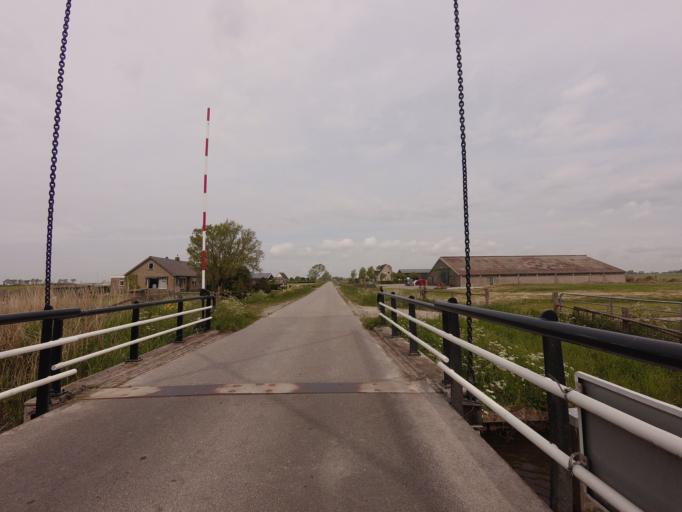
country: NL
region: Friesland
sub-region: Sudwest Fryslan
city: Makkum
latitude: 53.0632
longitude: 5.4613
